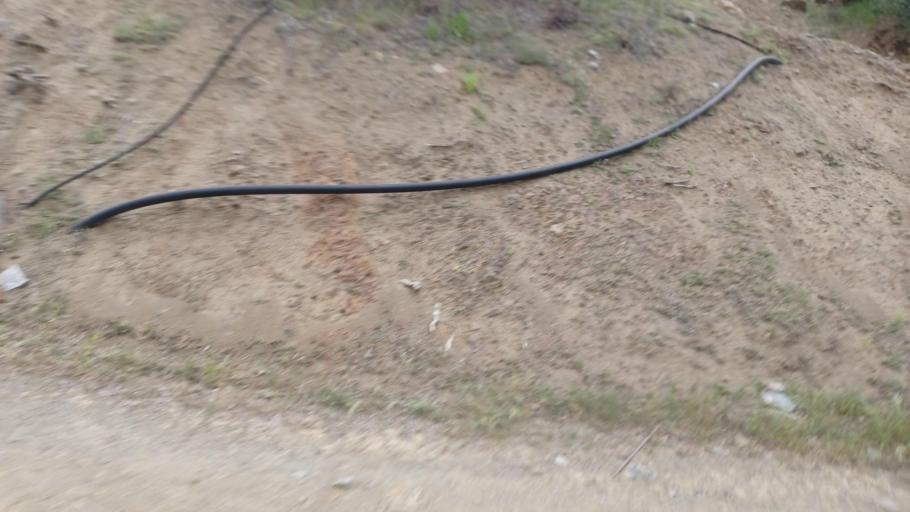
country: CY
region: Limassol
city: Pelendri
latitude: 34.8635
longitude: 33.0869
